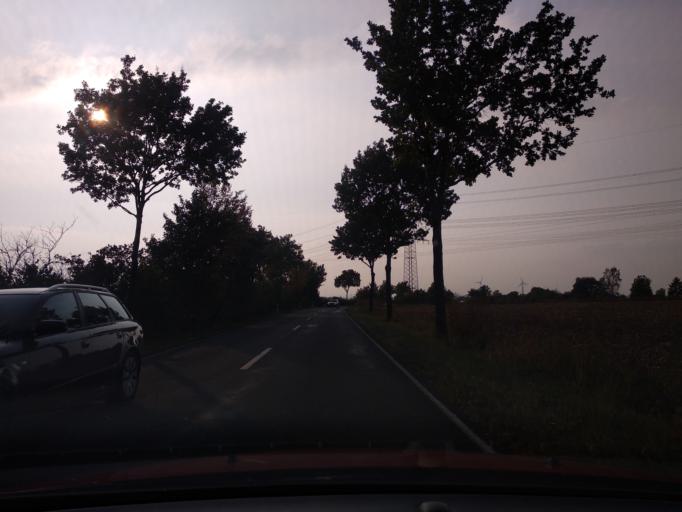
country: DE
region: North Rhine-Westphalia
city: Beverungen
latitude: 51.6292
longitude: 9.3402
